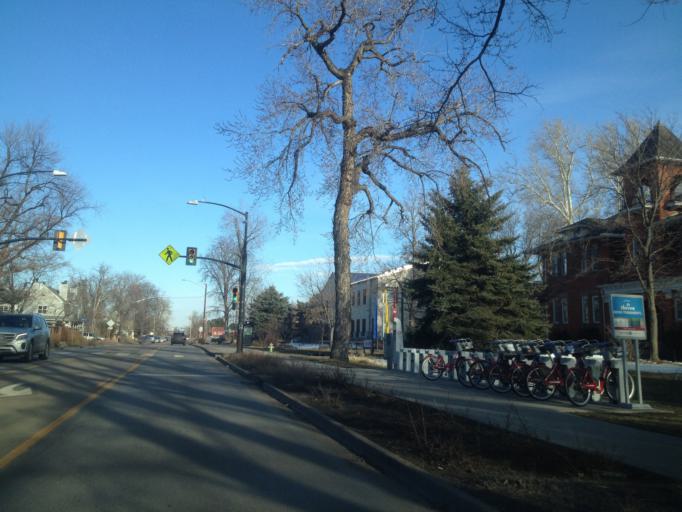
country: US
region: Colorado
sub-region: Boulder County
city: Boulder
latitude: 40.0146
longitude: -105.2676
